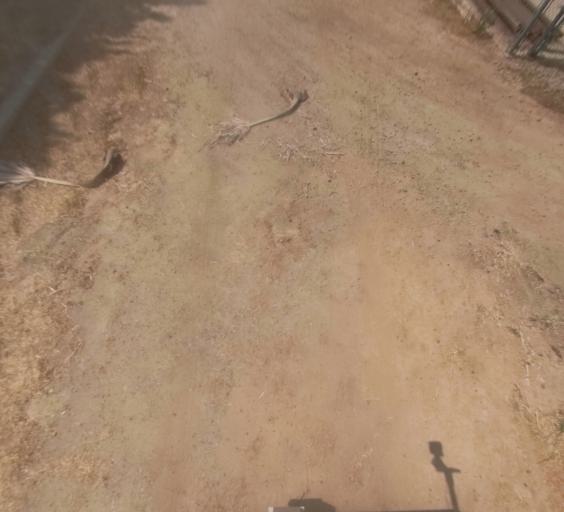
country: US
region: California
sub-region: Madera County
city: Fairmead
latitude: 37.0780
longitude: -120.1959
